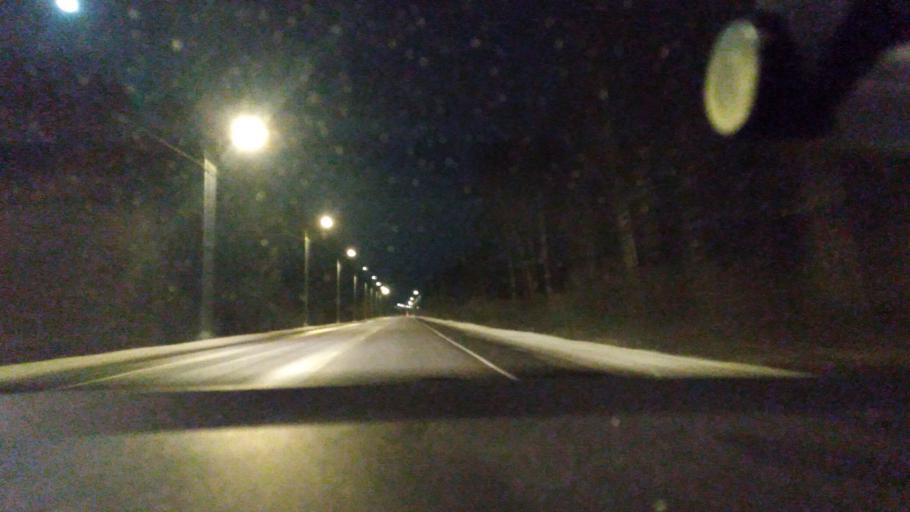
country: RU
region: Moskovskaya
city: Yegor'yevsk
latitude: 55.4524
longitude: 39.0006
